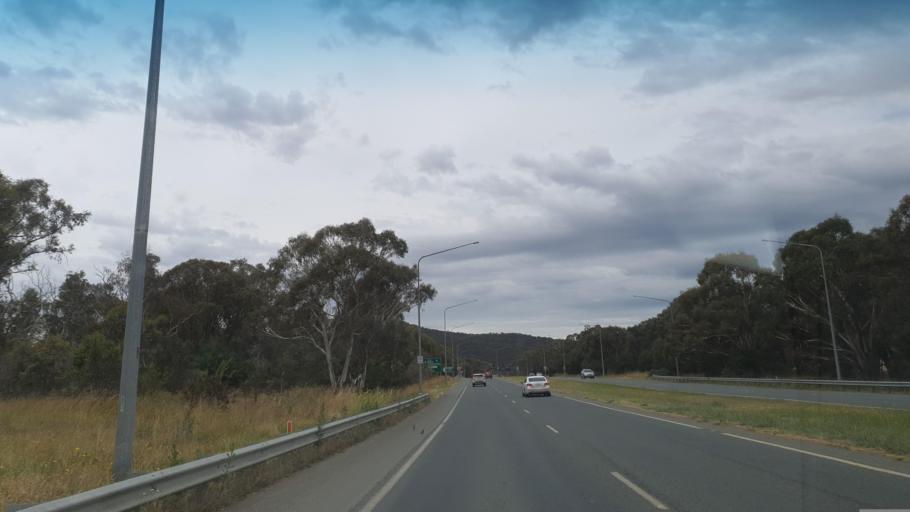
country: AU
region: Australian Capital Territory
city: Macquarie
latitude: -35.2763
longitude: 149.0724
